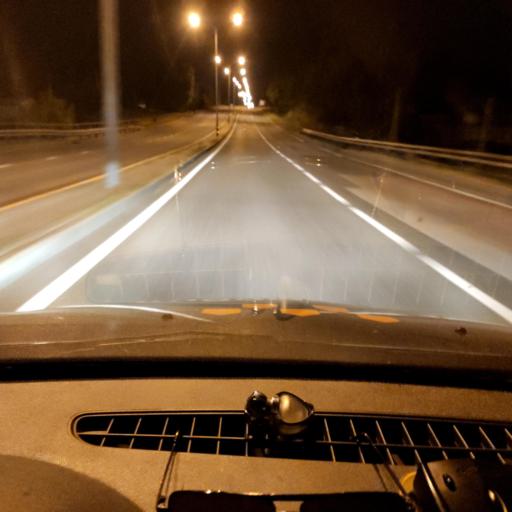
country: RU
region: Belgorod
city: Gubkin
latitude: 51.2681
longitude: 37.5657
